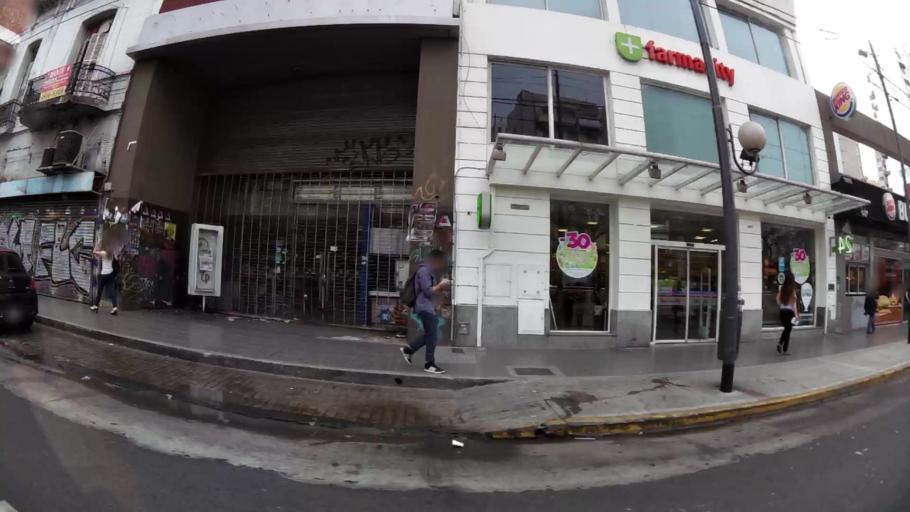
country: AR
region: Buenos Aires F.D.
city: Colegiales
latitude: -34.5538
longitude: -58.4636
